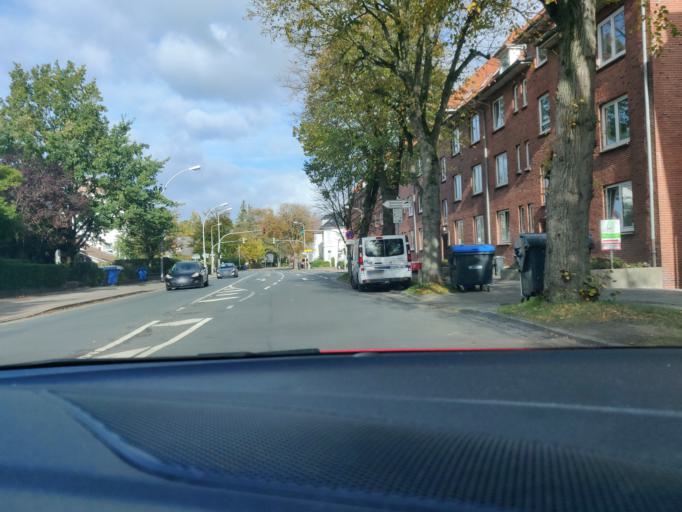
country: DE
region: Lower Saxony
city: Cuxhaven
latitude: 53.8580
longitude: 8.6936
